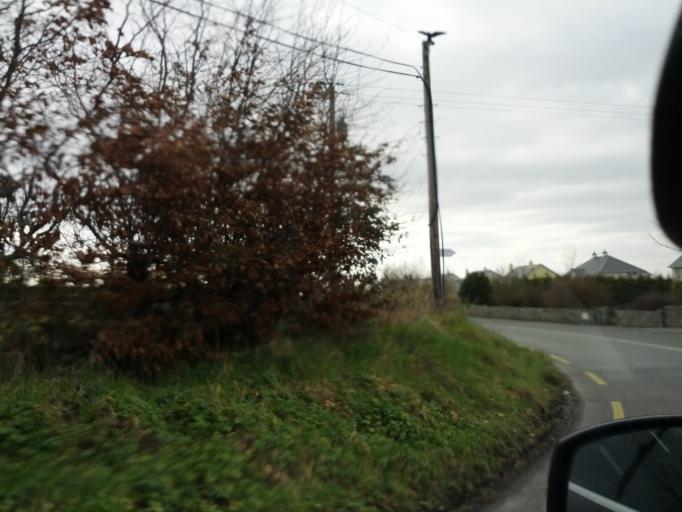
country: IE
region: Connaught
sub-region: County Galway
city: Oranmore
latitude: 53.2099
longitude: -8.8349
